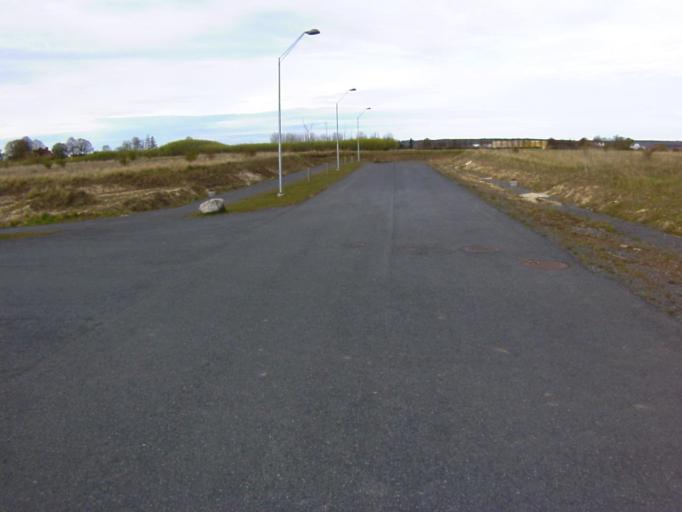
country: SE
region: Skane
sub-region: Kristianstads Kommun
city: Kristianstad
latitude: 56.0258
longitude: 14.1154
